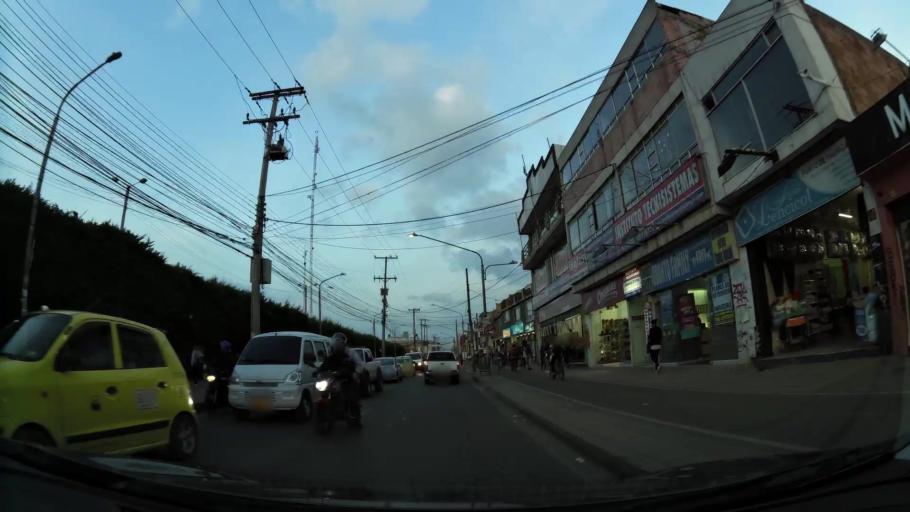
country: CO
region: Cundinamarca
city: Funza
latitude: 4.7141
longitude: -74.2171
